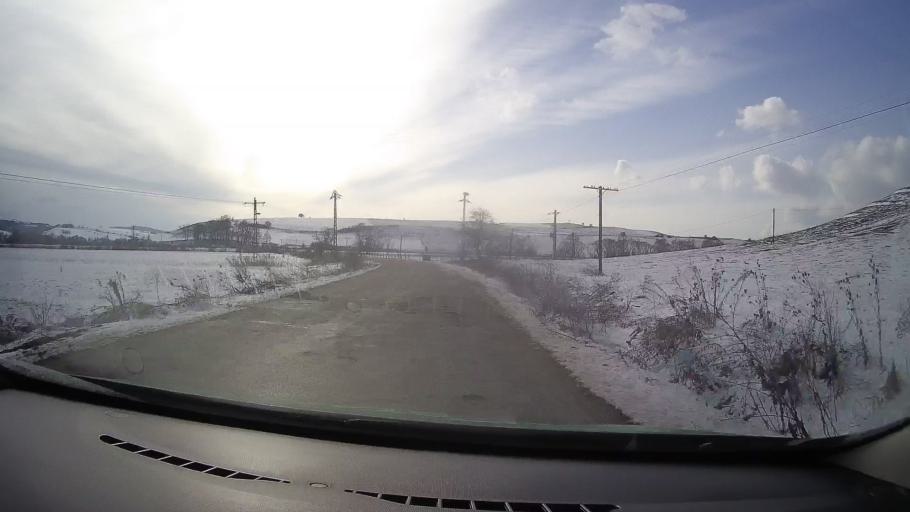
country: RO
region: Sibiu
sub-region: Comuna Iacobeni
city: Iacobeni
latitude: 46.0276
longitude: 24.7097
